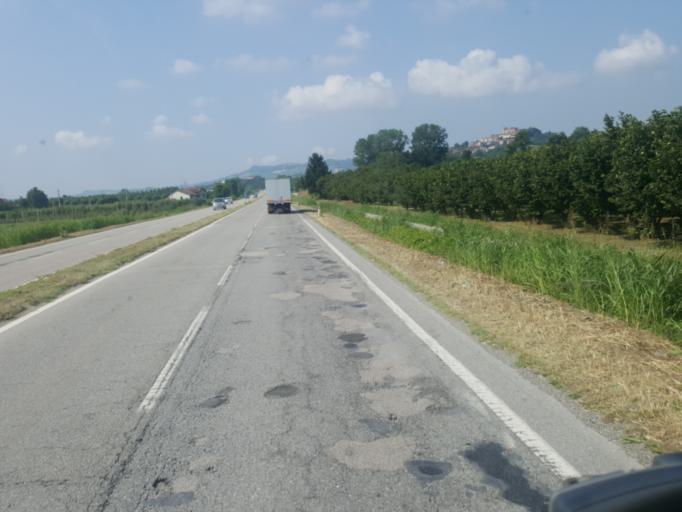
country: IT
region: Piedmont
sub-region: Provincia di Cuneo
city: Roddi
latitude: 44.6869
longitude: 7.9954
